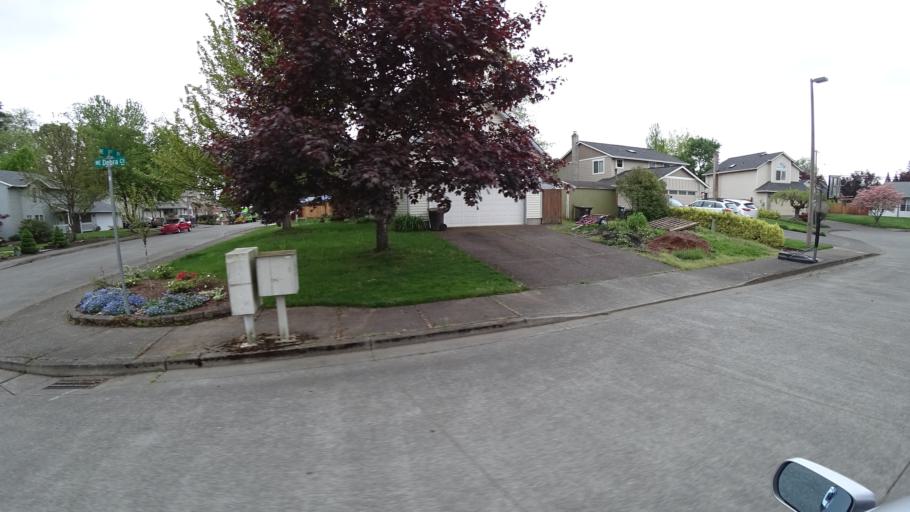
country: US
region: Oregon
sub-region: Washington County
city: Hillsboro
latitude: 45.5321
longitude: -122.9884
